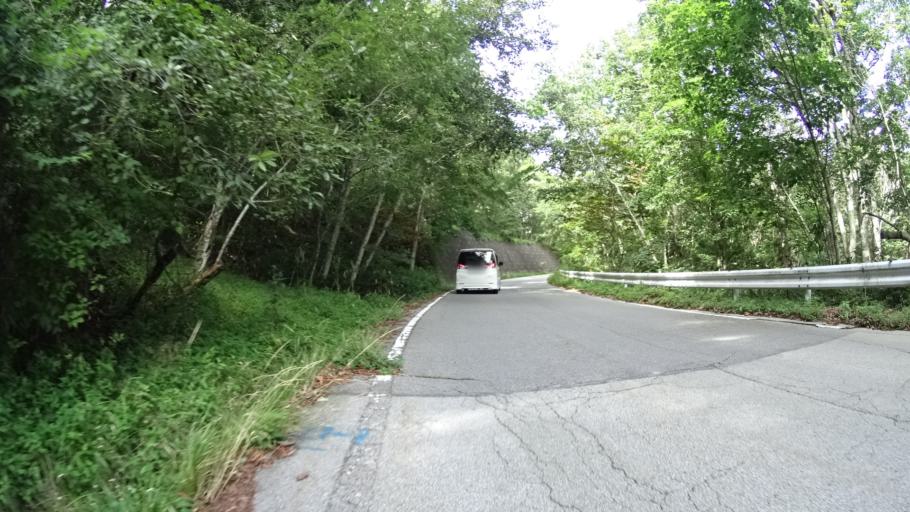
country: JP
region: Yamanashi
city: Nirasaki
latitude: 35.9138
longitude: 138.5419
